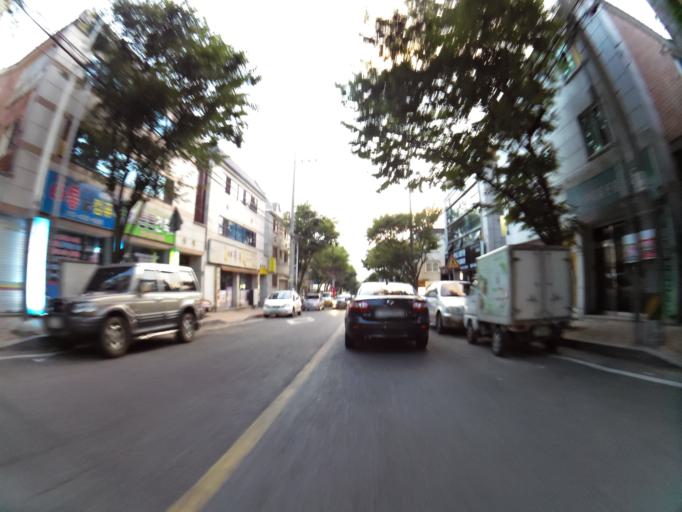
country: KR
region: Gyeongsangbuk-do
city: Gyeongsan-si
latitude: 35.8428
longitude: 128.7493
